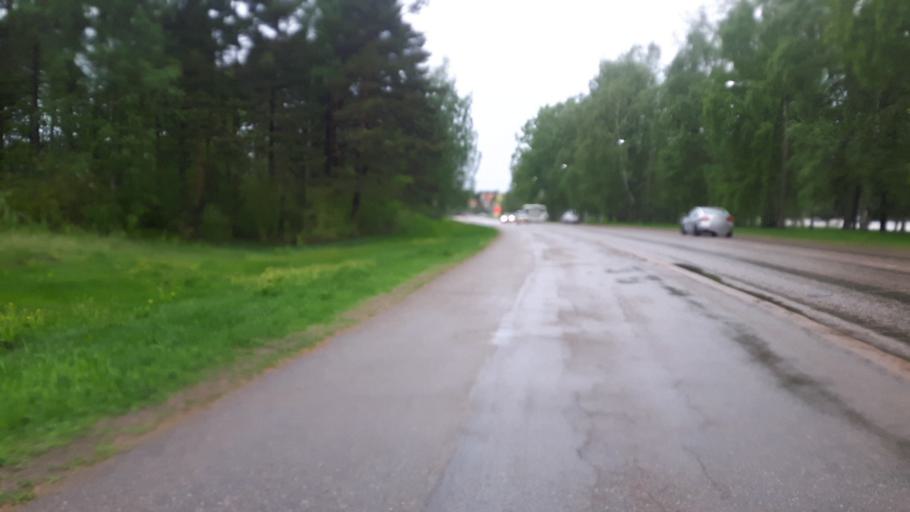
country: FI
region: Kymenlaakso
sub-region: Kotka-Hamina
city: Kotka
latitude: 60.4836
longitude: 26.9096
